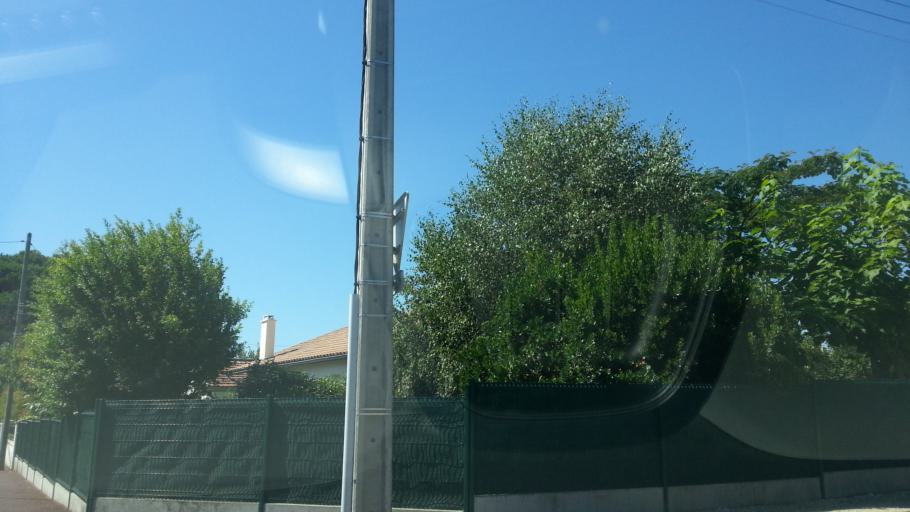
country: FR
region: Aquitaine
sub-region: Departement de la Gironde
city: Villenave-d'Ornon
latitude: 44.7635
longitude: -0.5708
